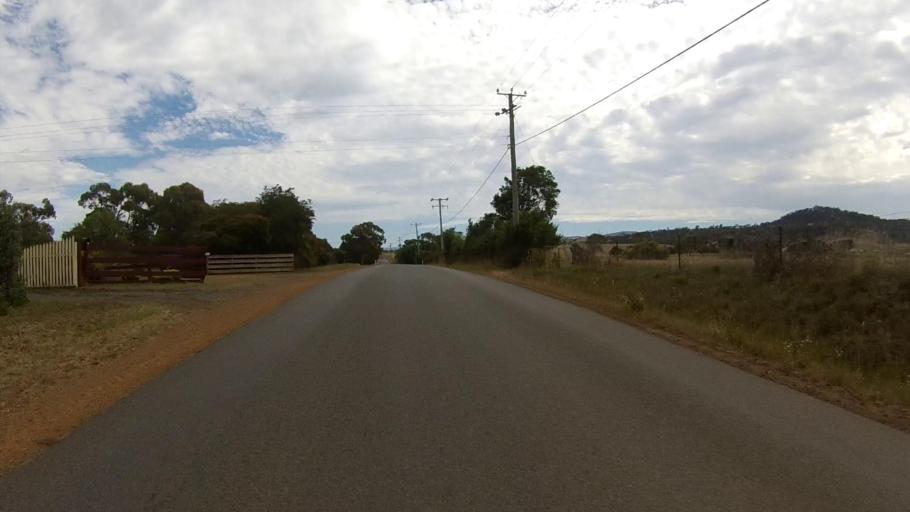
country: AU
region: Tasmania
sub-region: Clarence
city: Cambridge
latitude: -42.7319
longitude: 147.4484
